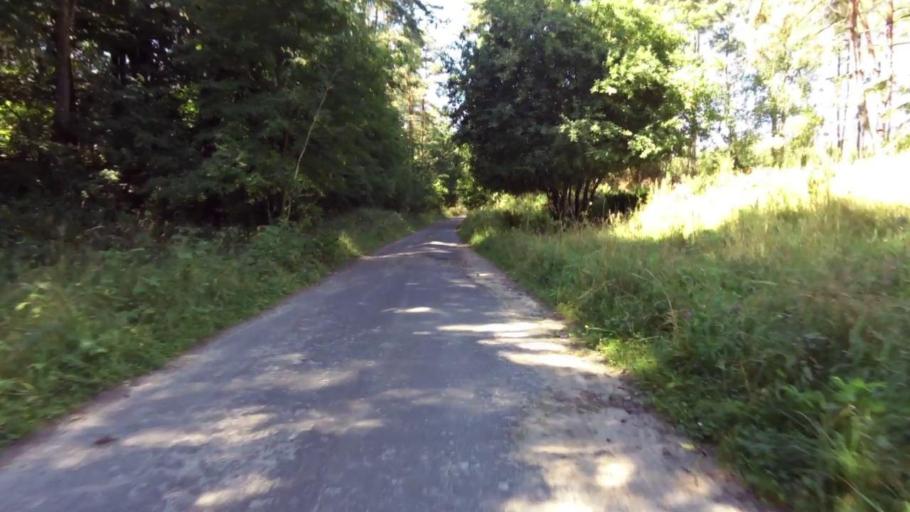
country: PL
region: West Pomeranian Voivodeship
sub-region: Powiat szczecinecki
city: Szczecinek
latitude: 53.5928
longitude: 16.6614
